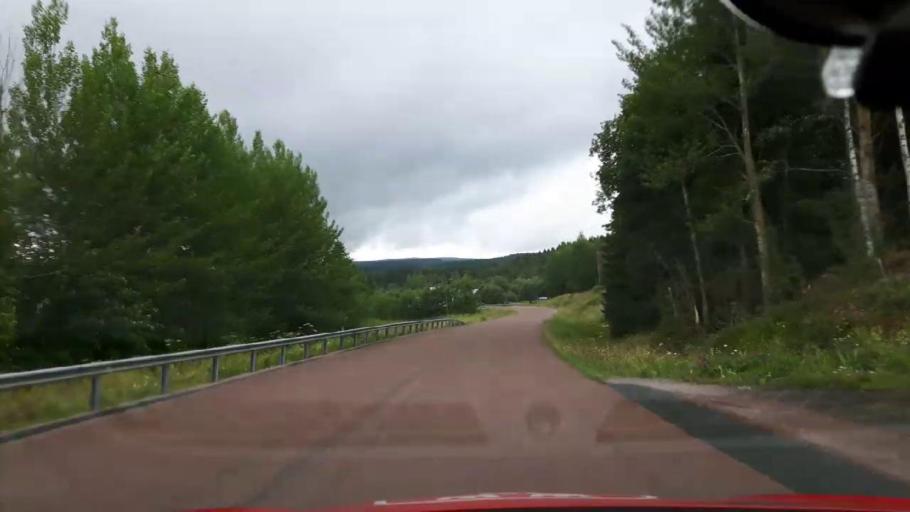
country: SE
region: Jaemtland
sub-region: Krokoms Kommun
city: Valla
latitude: 63.3820
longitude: 13.7684
